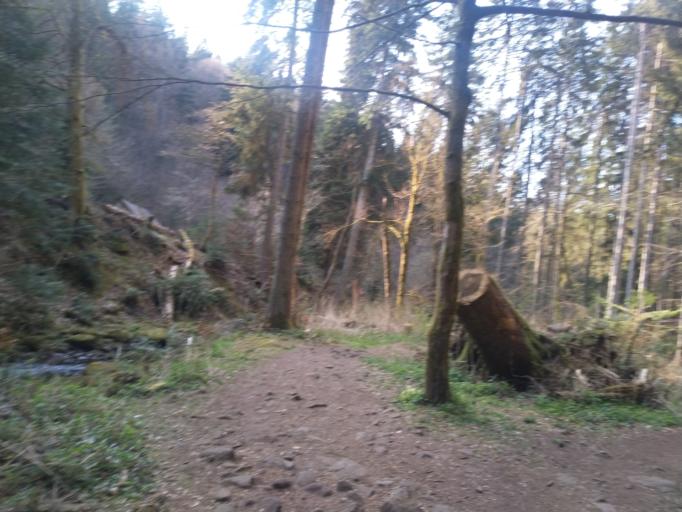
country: DE
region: Baden-Wuerttemberg
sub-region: Karlsruhe Region
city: Bad Liebenzell
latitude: 48.8000
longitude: 8.7435
